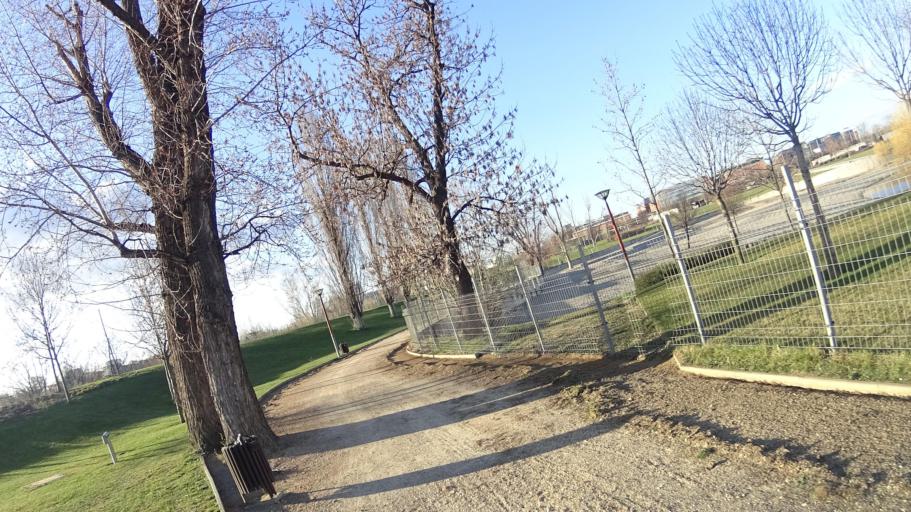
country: HU
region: Budapest
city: Budapest IX. keruelet
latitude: 47.4655
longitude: 19.0593
